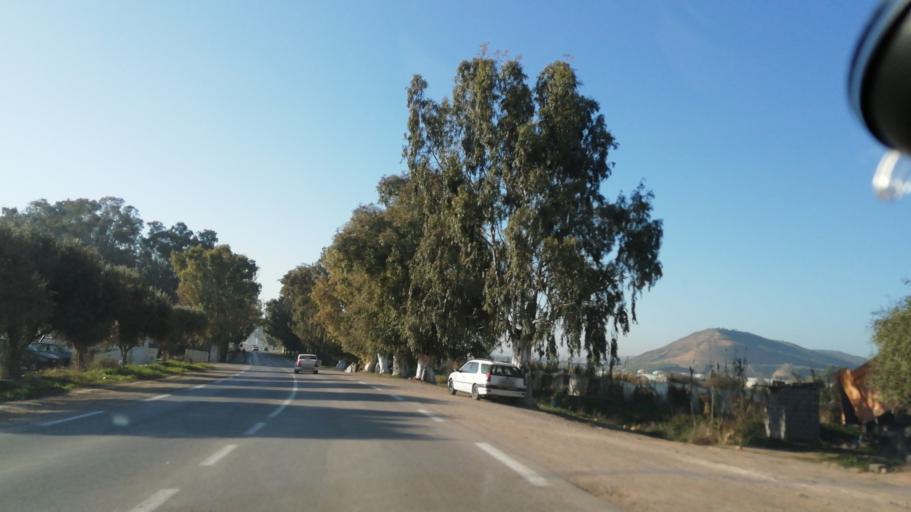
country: DZ
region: Tlemcen
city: Remchi
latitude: 35.0540
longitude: -1.5016
